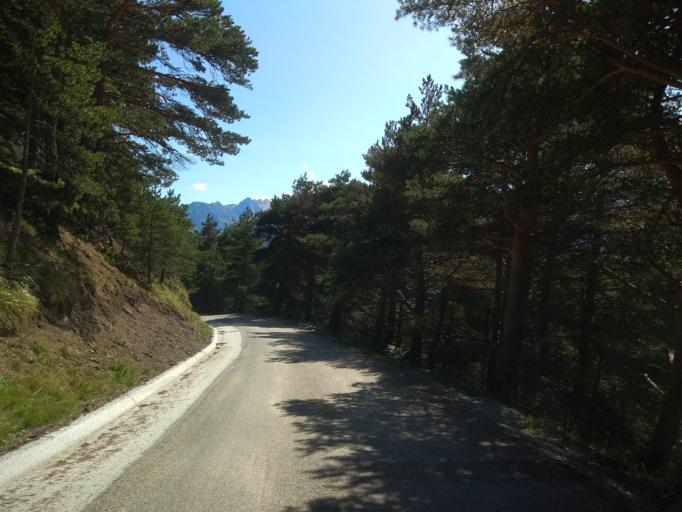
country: ES
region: Catalonia
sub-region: Provincia de Lleida
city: Les
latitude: 42.7679
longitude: 0.7132
